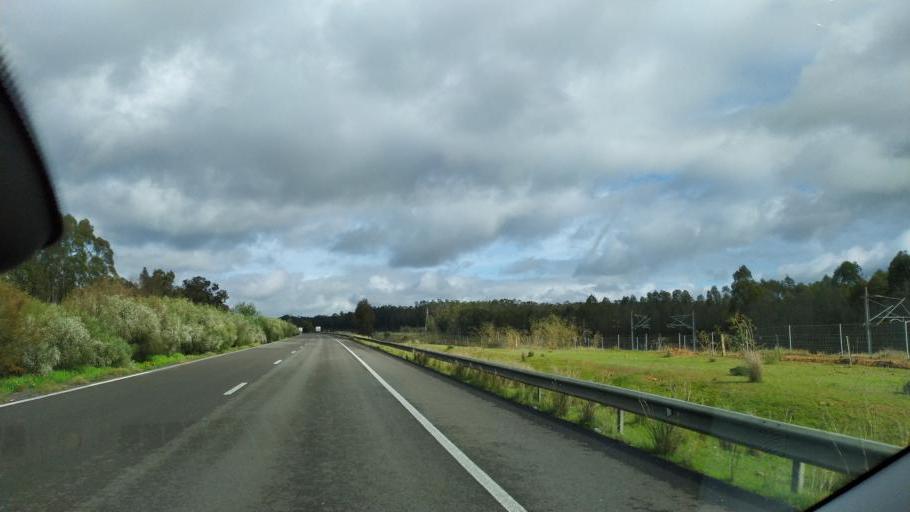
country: MA
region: Gharb-Chrarda-Beni Hssen
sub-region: Kenitra Province
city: Lalla Mimouna
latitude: 34.9159
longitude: -6.2054
